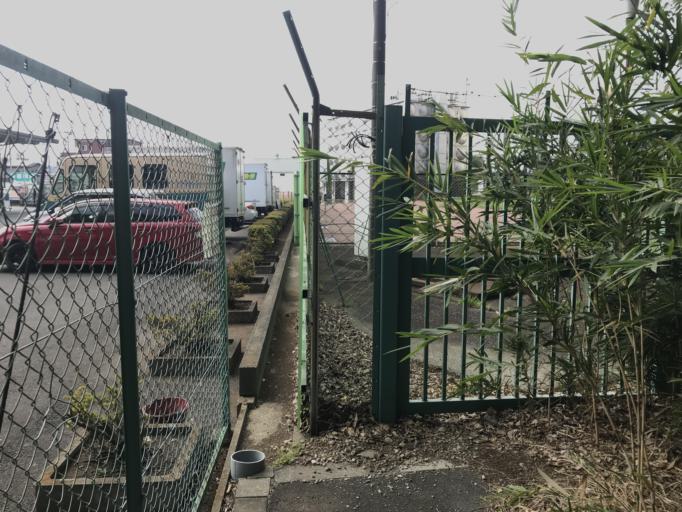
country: JP
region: Saitama
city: Asaka
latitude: 35.7790
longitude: 139.5567
